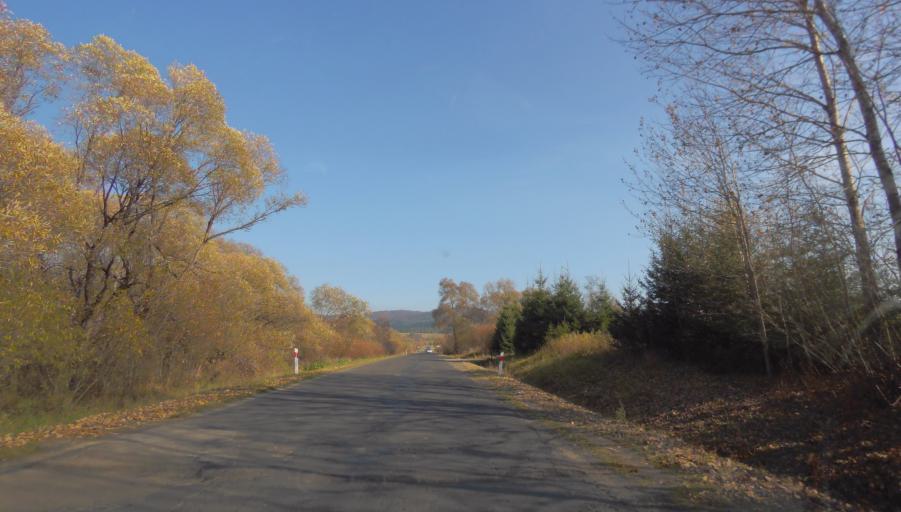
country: PL
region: Subcarpathian Voivodeship
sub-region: Powiat sanocki
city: Komancza
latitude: 49.2436
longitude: 22.1129
